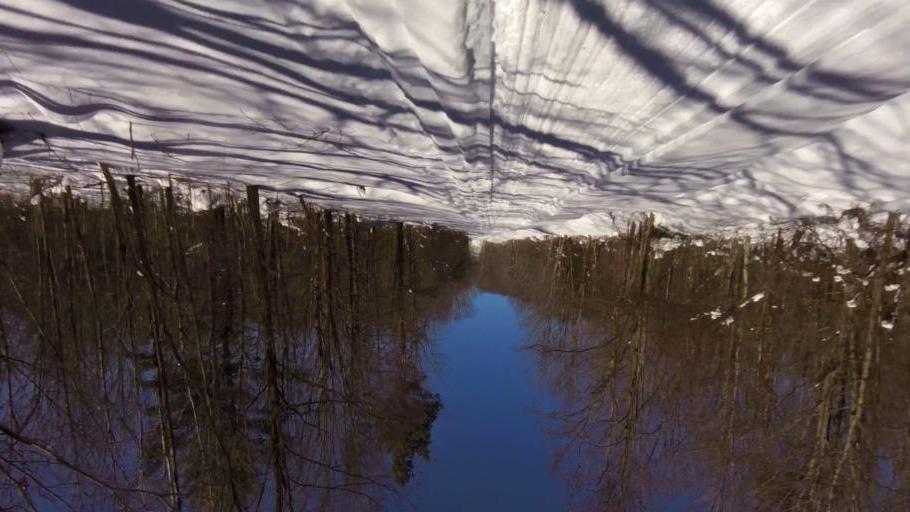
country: US
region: New York
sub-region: Allegany County
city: Cuba
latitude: 42.3146
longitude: -78.2310
